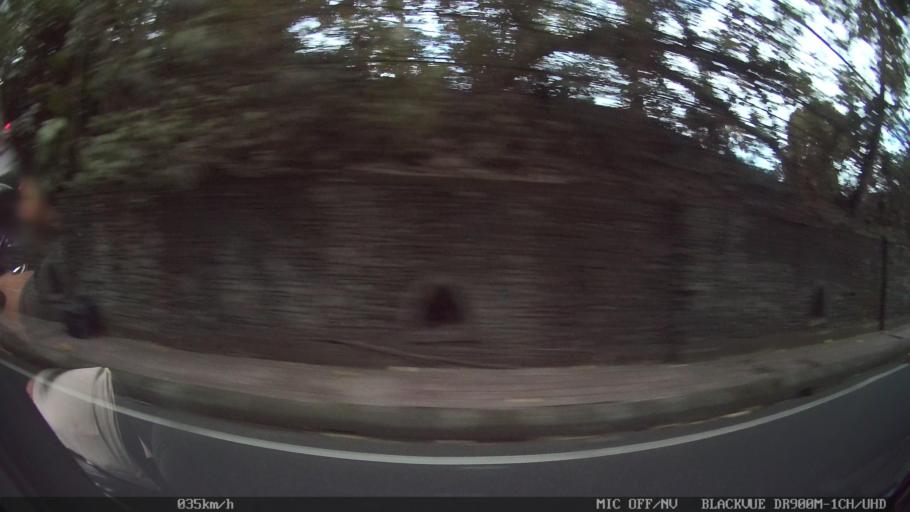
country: ID
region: Bali
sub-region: Kabupaten Gianyar
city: Ubud
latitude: -8.5017
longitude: 115.2527
